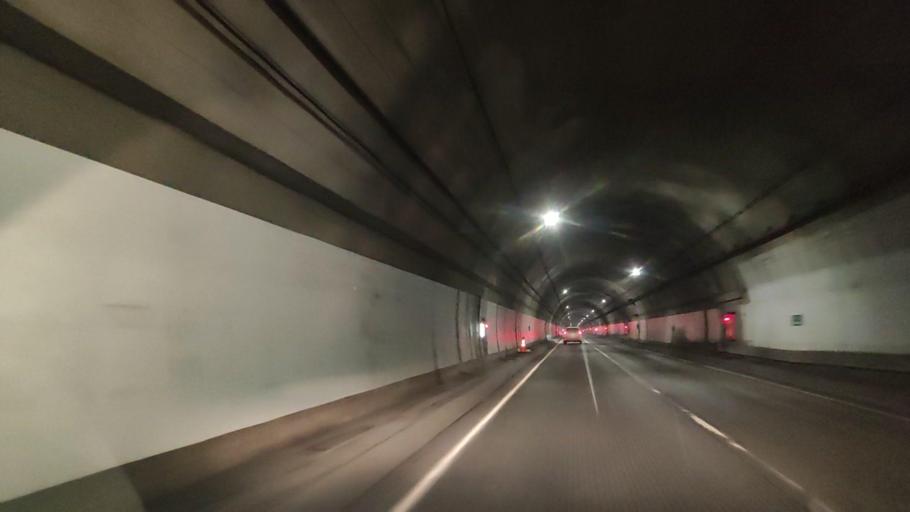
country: JP
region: Hokkaido
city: Rumoi
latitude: 43.7105
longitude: 141.3323
